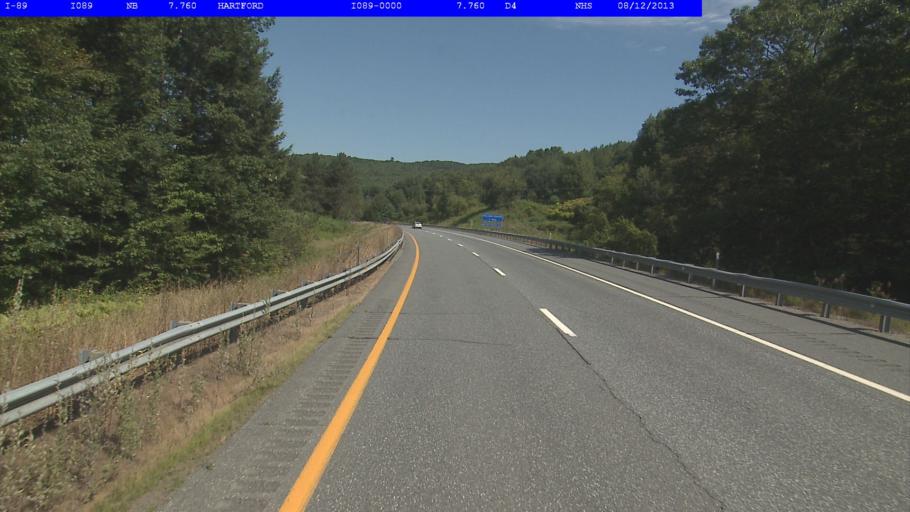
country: US
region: Vermont
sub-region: Windsor County
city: Wilder
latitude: 43.7166
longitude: -72.4124
